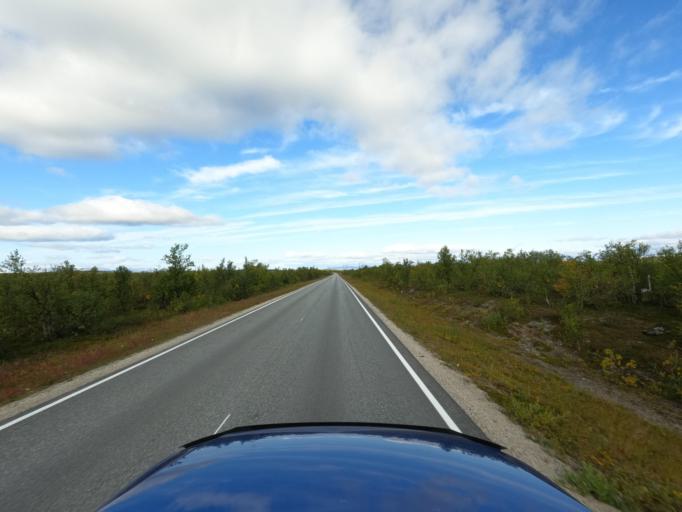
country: NO
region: Finnmark Fylke
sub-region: Karasjok
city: Karasjohka
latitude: 69.6588
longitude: 25.2772
